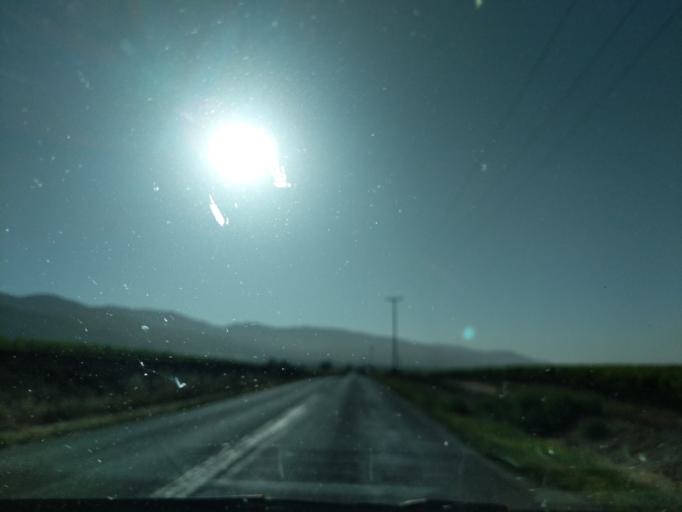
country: US
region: California
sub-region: Monterey County
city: Soledad
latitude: 36.4294
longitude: -121.4086
